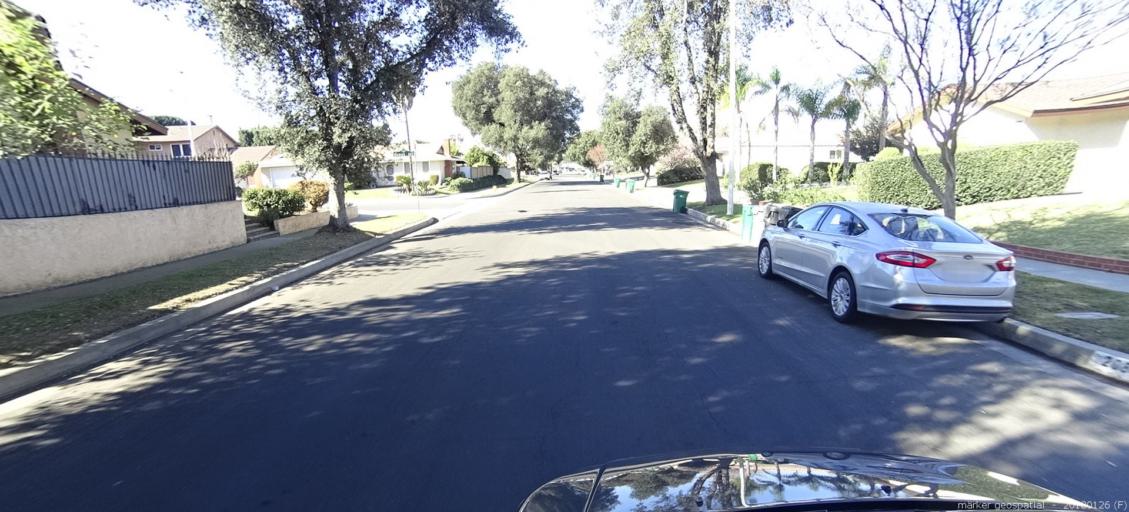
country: US
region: California
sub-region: Los Angeles County
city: Walnut
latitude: 34.0020
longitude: -117.8496
